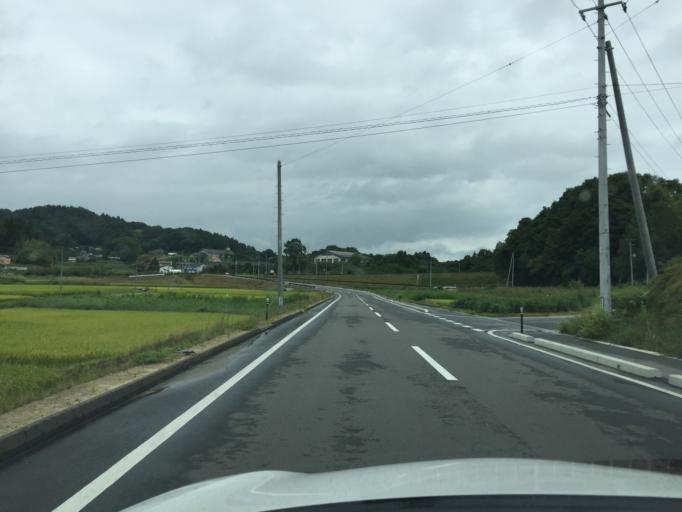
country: JP
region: Fukushima
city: Funehikimachi-funehiki
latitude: 37.4475
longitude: 140.5584
